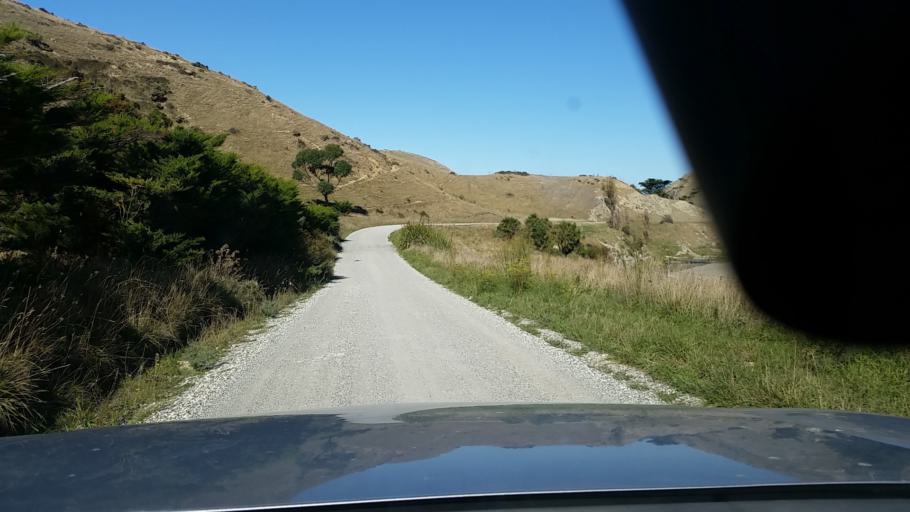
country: NZ
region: Marlborough
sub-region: Marlborough District
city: Blenheim
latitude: -41.8391
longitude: 174.1812
